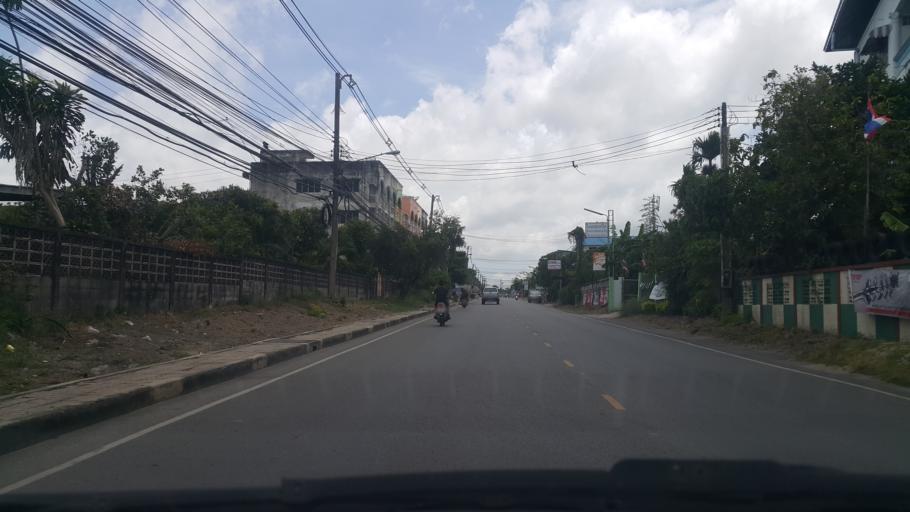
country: TH
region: Rayong
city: Ban Chang
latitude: 12.7306
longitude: 101.0503
